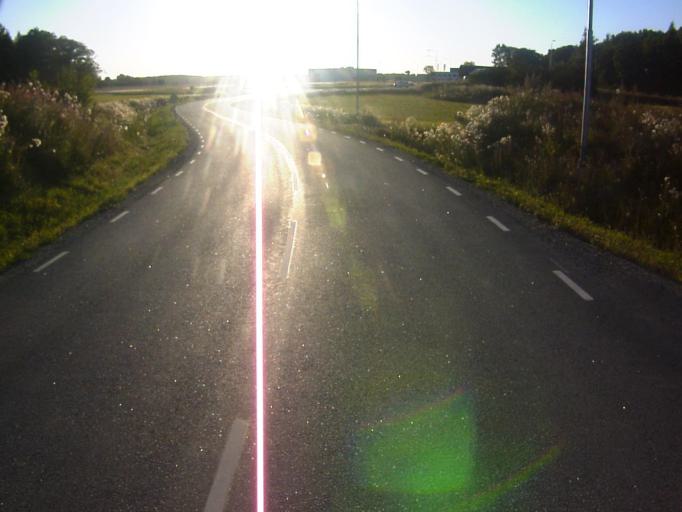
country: SE
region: Soedermanland
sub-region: Eskilstuna Kommun
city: Hallbybrunn
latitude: 59.4073
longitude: 16.4339
